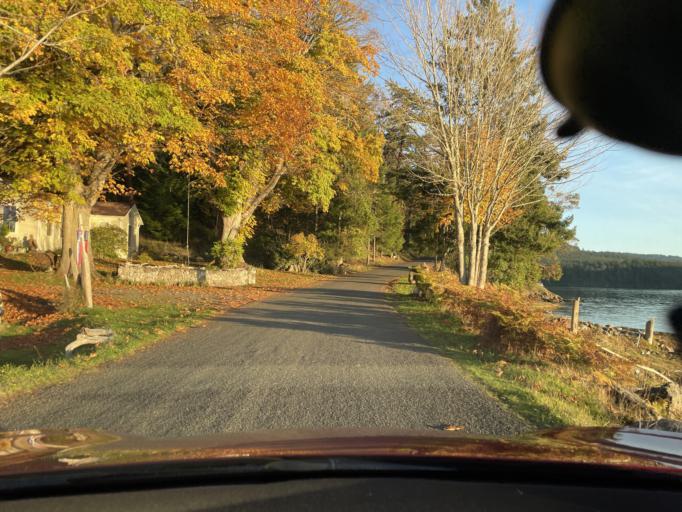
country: US
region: Washington
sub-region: San Juan County
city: Friday Harbor
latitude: 48.6004
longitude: -123.1579
